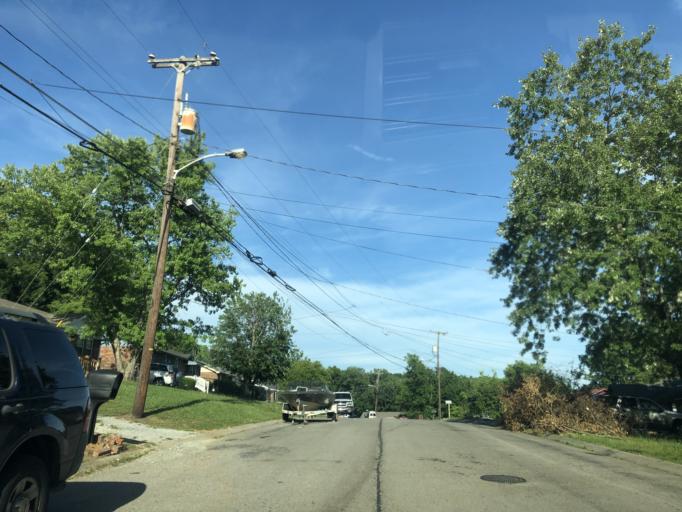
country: US
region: Tennessee
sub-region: Davidson County
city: Nashville
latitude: 36.2240
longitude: -86.8462
